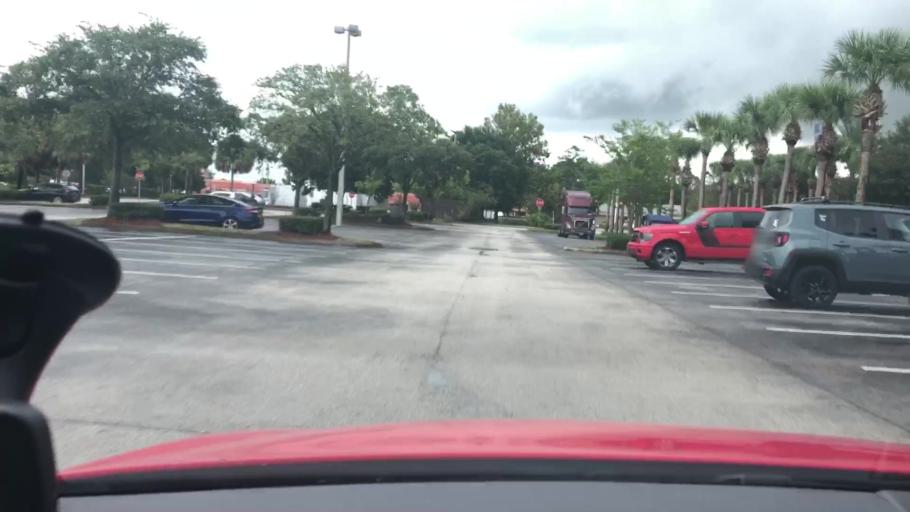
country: US
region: Florida
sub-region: Volusia County
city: Daytona Beach
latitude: 29.1784
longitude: -81.0832
